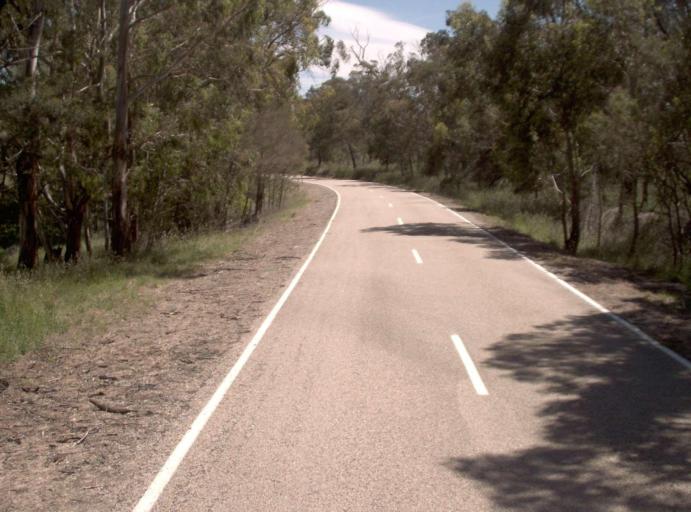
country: AU
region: Victoria
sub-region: East Gippsland
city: Lakes Entrance
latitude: -37.2739
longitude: 148.2559
